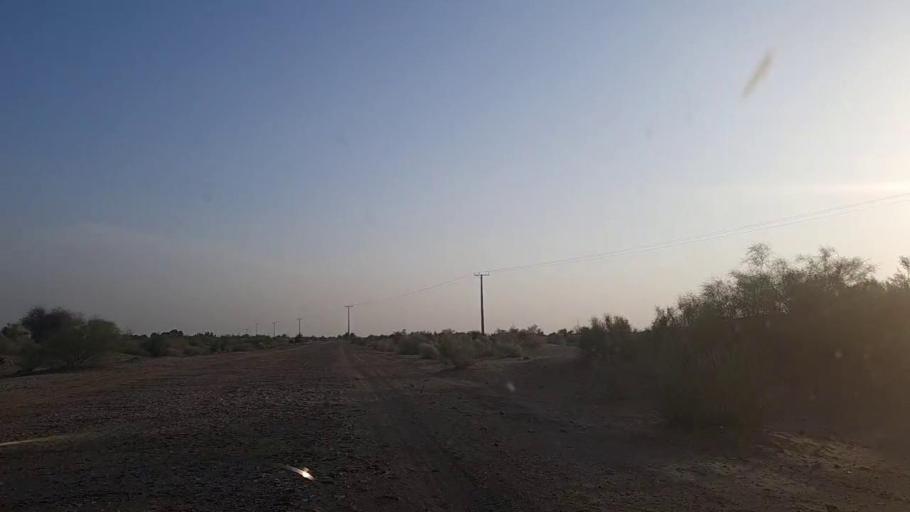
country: PK
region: Sindh
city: Khanpur
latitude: 27.6431
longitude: 69.4569
